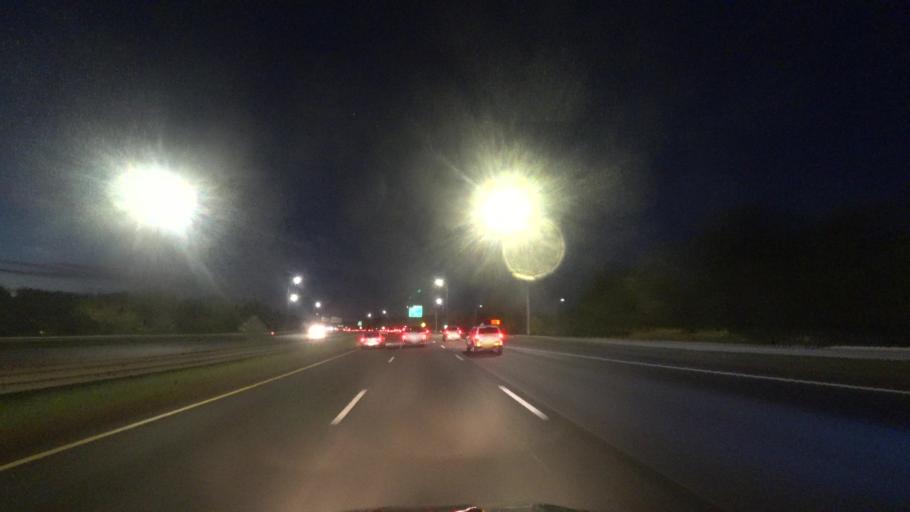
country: US
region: Massachusetts
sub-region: Essex County
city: North Andover
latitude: 42.6977
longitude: -71.1422
